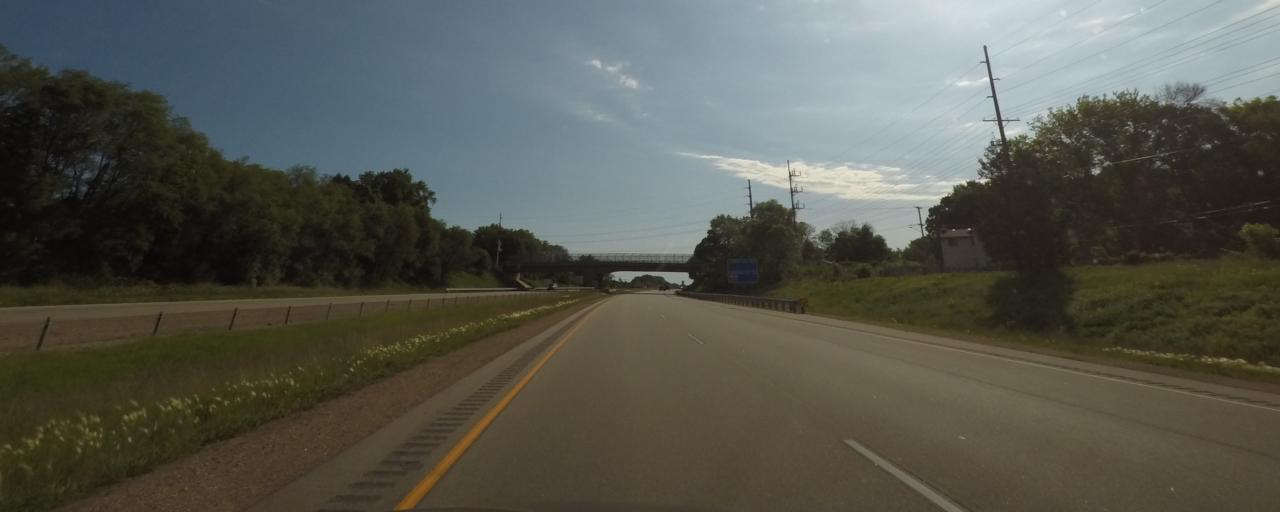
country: US
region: Wisconsin
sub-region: Dane County
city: Sun Prairie
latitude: 43.1904
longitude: -89.2276
